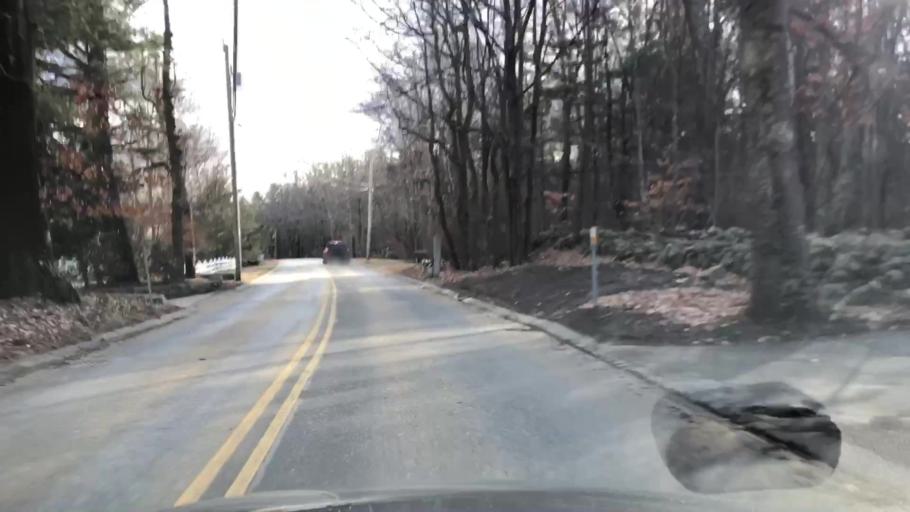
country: US
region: New Hampshire
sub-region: Hillsborough County
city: Mont Vernon
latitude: 42.8854
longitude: -71.6318
